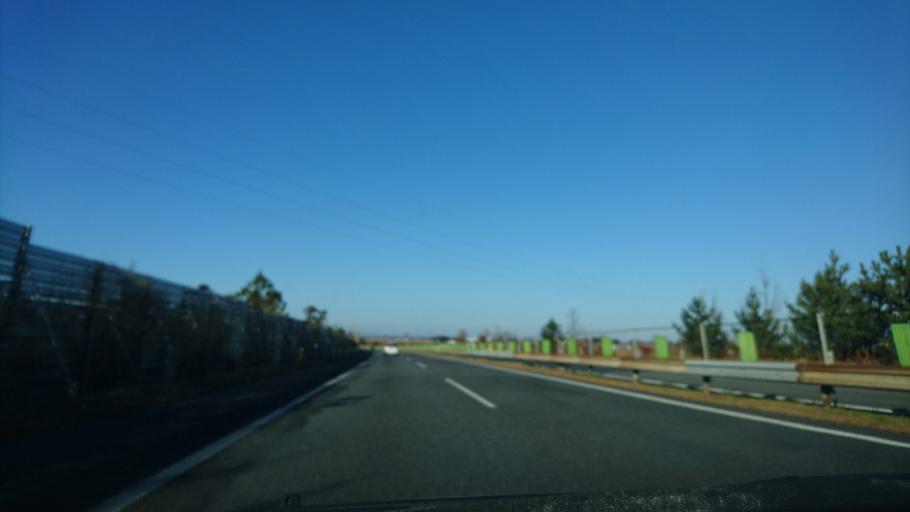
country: JP
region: Miyagi
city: Furukawa
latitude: 38.5527
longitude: 140.9314
